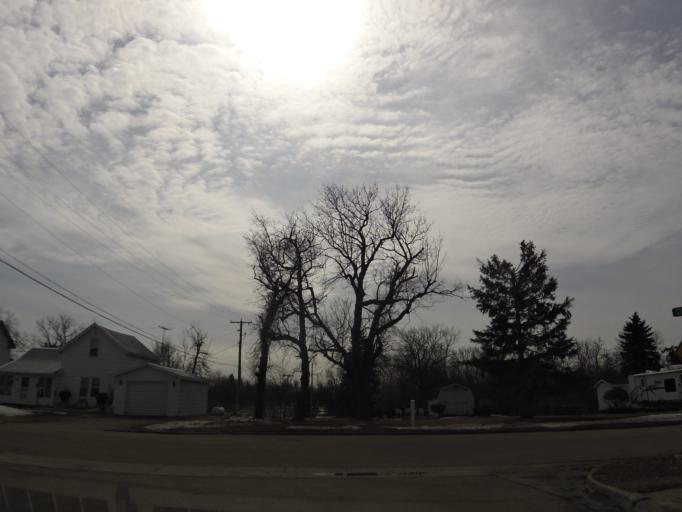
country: US
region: North Dakota
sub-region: Walsh County
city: Grafton
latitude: 48.2896
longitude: -97.3730
